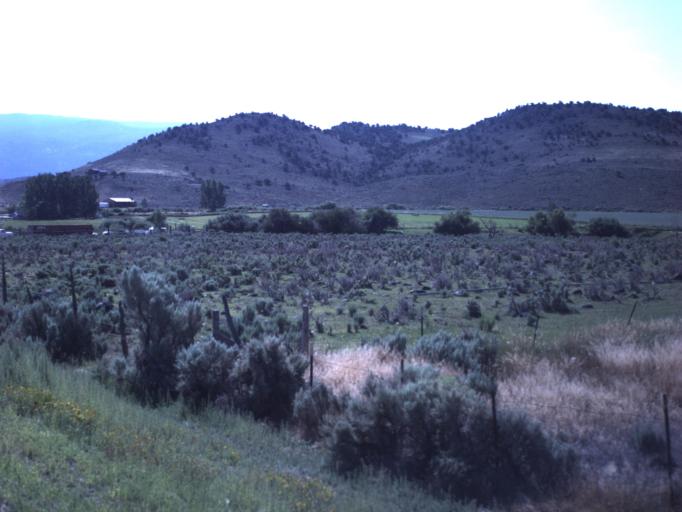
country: US
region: Utah
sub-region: Wayne County
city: Loa
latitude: 38.4622
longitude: -111.6015
